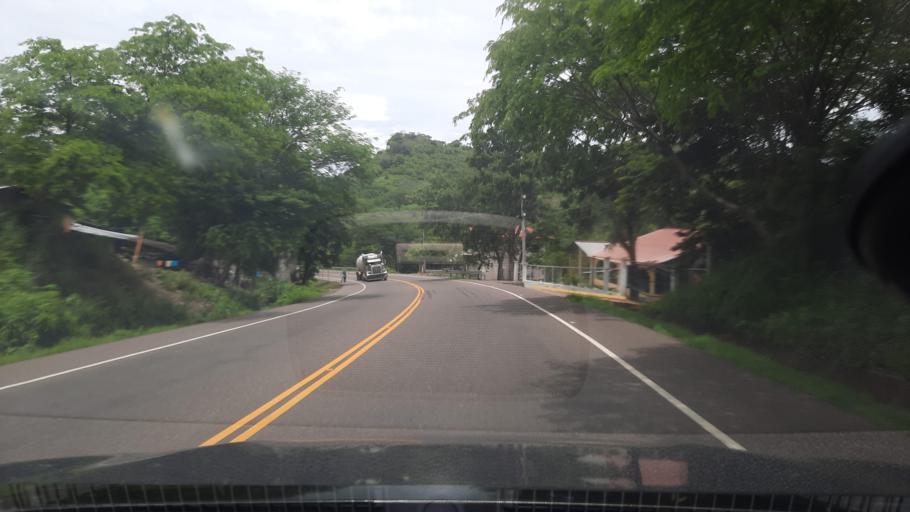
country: HN
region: Valle
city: Langue
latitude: 13.5796
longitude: -87.6854
